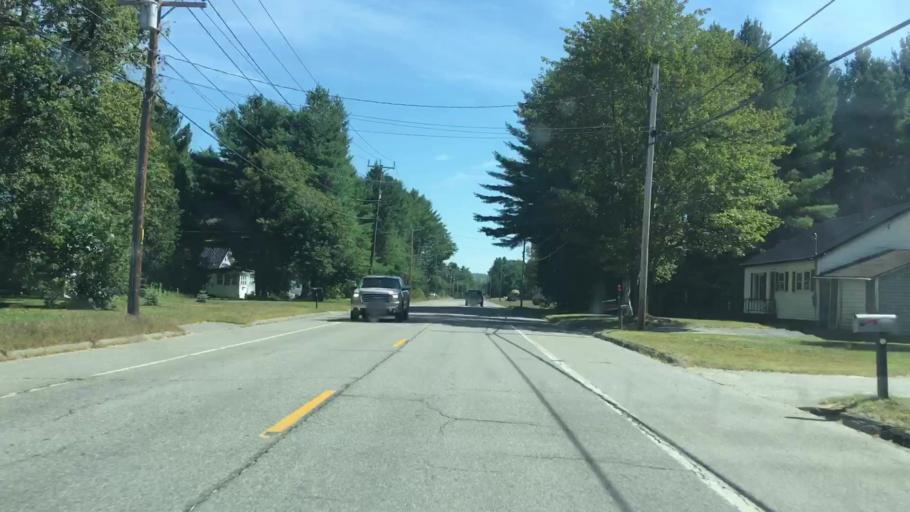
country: US
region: Maine
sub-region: Piscataquis County
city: Milo
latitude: 45.2404
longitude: -68.9691
